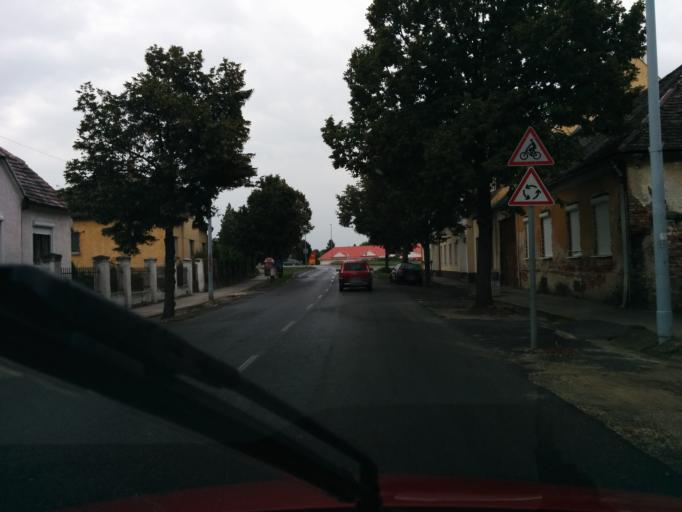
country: HU
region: Vas
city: Koszeg
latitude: 47.3816
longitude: 16.5532
